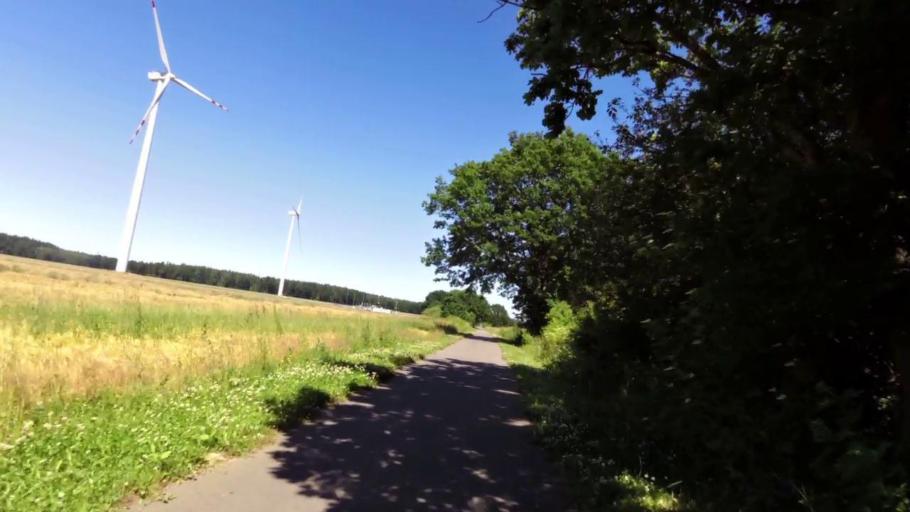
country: PL
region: West Pomeranian Voivodeship
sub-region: Powiat kolobrzeski
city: Goscino
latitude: 54.0318
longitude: 15.7033
